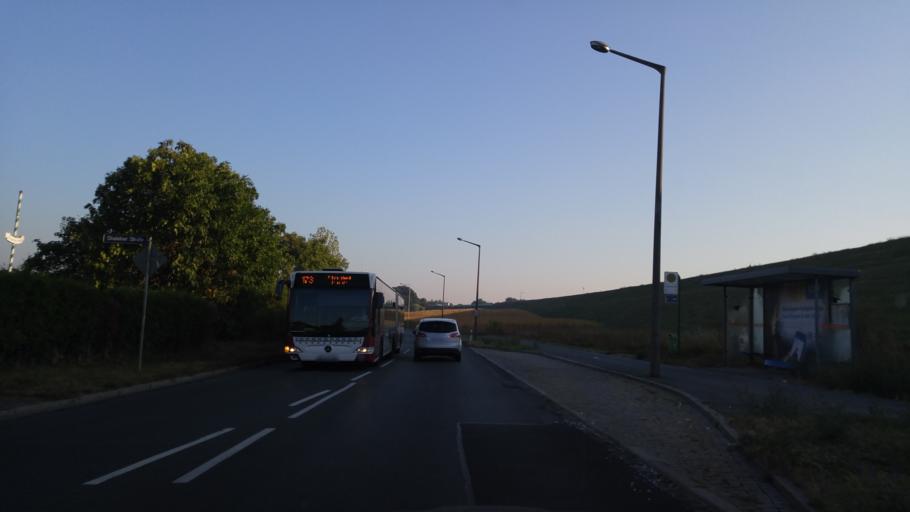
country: DE
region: Bavaria
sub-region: Regierungsbezirk Mittelfranken
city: Furth
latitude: 49.5071
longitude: 10.9574
